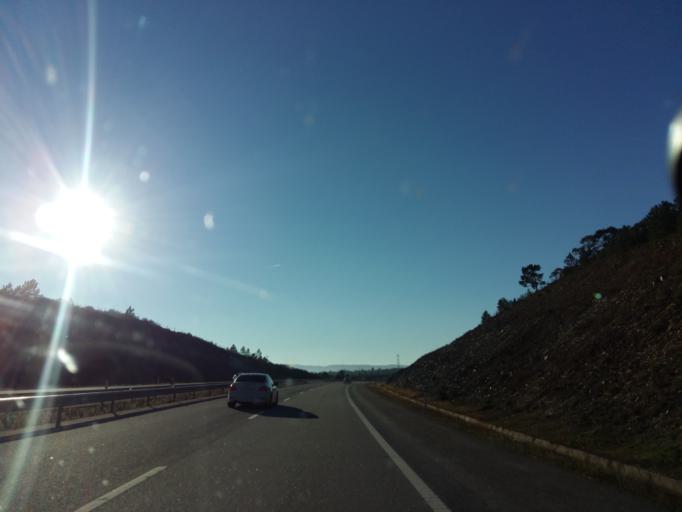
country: ES
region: Extremadura
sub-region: Provincia de Caceres
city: Cedillo
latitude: 39.7347
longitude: -7.6578
